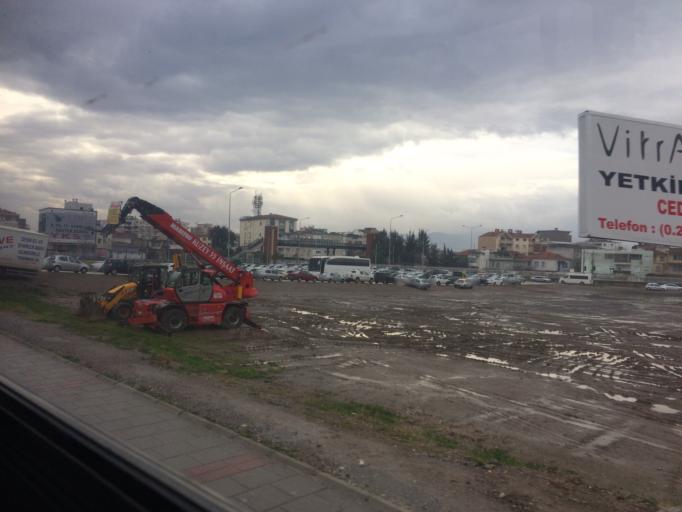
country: TR
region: Izmir
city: Karsiyaka
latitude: 38.4958
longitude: 27.0600
